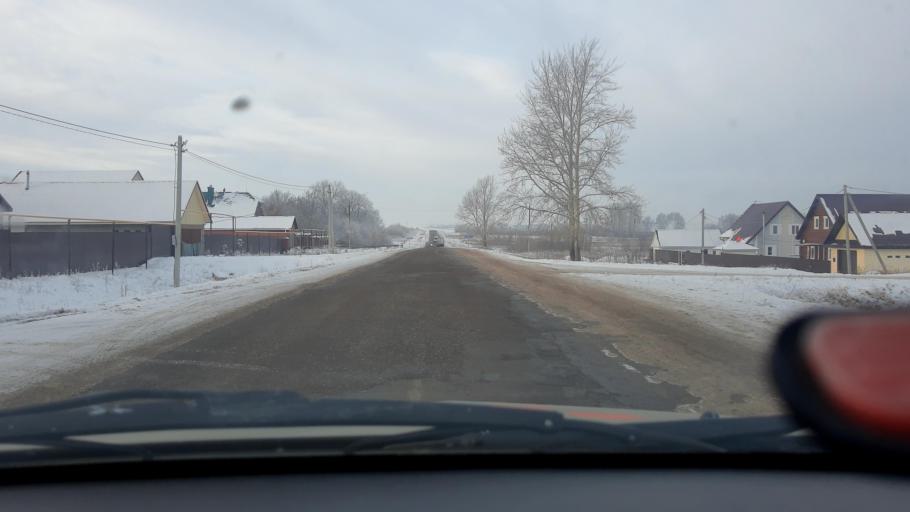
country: RU
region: Bashkortostan
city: Avdon
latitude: 54.3633
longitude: 55.8336
